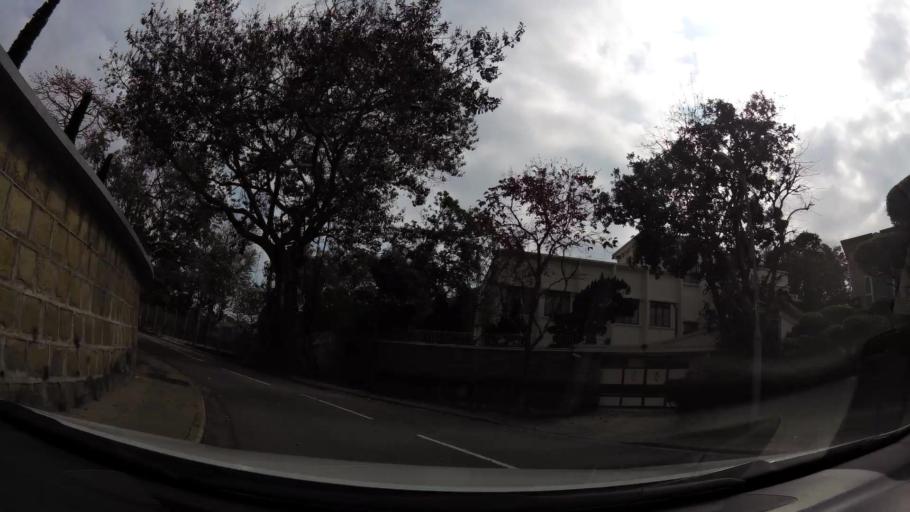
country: HK
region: Wanchai
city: Wan Chai
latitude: 22.2679
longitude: 114.1911
